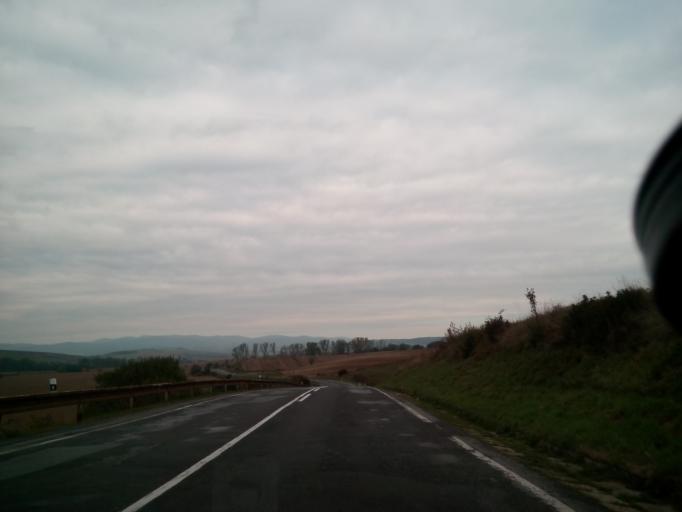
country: SK
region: Presovsky
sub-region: Okres Presov
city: Presov
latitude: 49.0738
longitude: 21.3292
